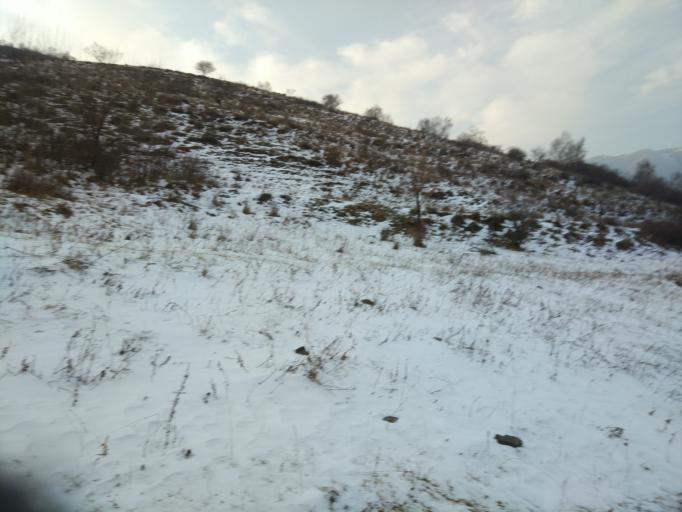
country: CN
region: Hebei
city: Xiwanzi
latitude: 40.7991
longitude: 115.4587
